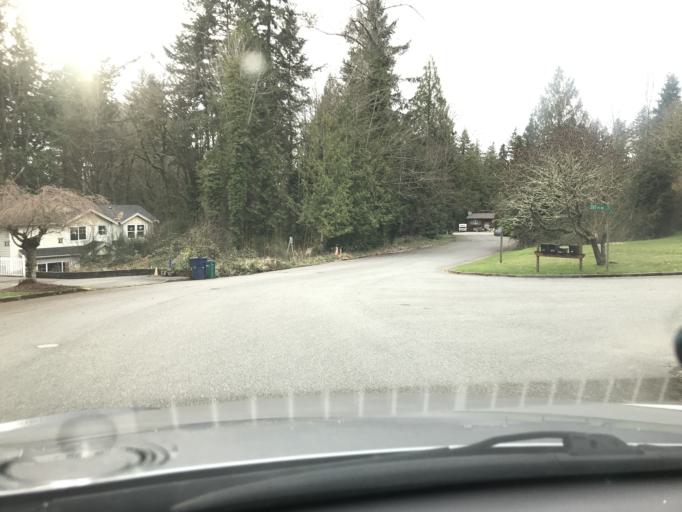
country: US
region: Washington
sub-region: King County
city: Union Hill-Novelty Hill
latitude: 47.6741
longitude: -122.0634
